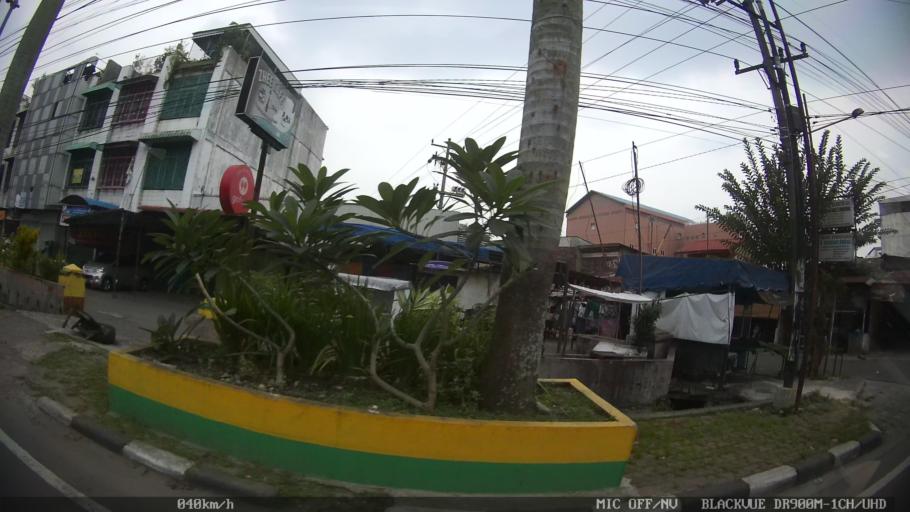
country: ID
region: North Sumatra
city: Medan
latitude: 3.5725
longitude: 98.6883
